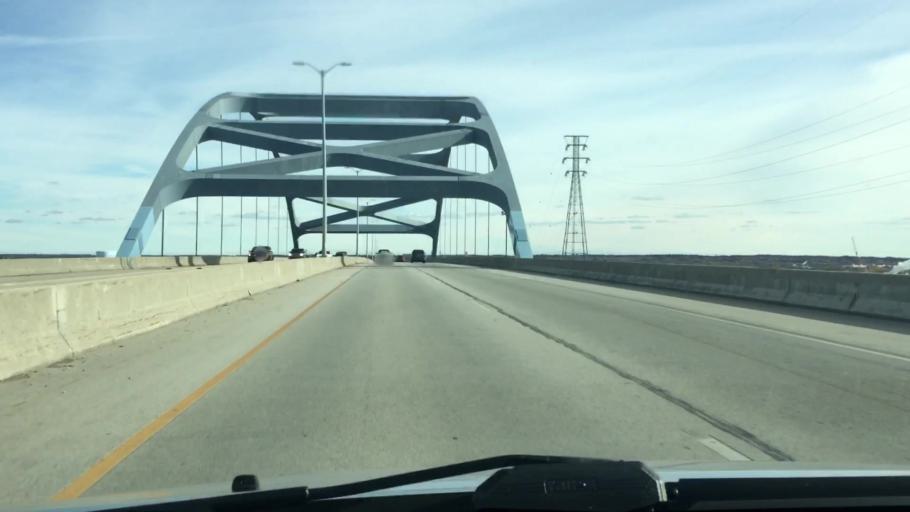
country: US
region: Wisconsin
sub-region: Brown County
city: Green Bay
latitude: 44.5337
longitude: -88.0092
